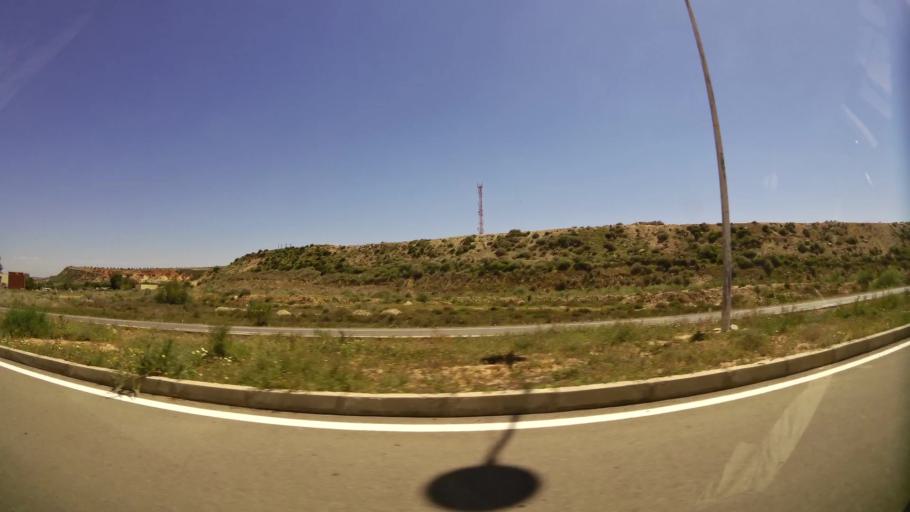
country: MA
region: Oriental
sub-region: Berkane-Taourirt
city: Madagh
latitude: 35.1000
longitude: -2.3273
